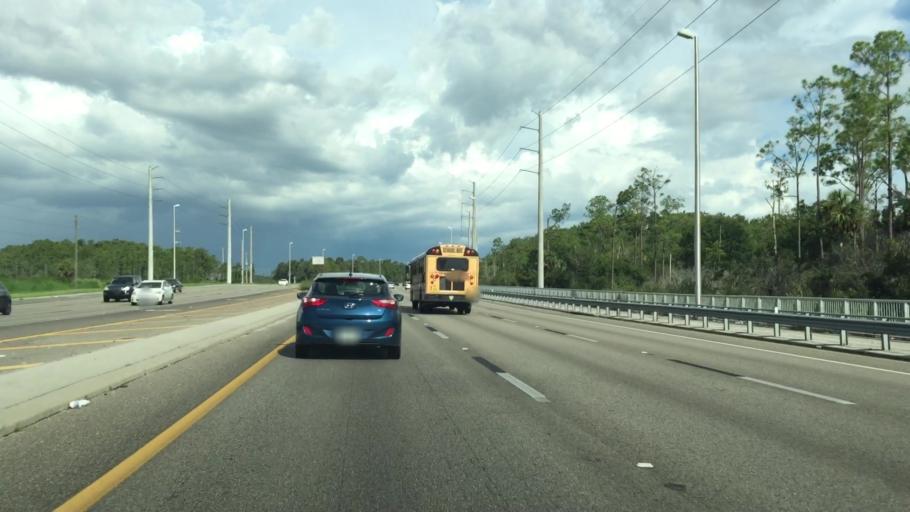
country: US
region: Florida
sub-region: Lee County
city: Tice
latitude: 26.6298
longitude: -81.7808
